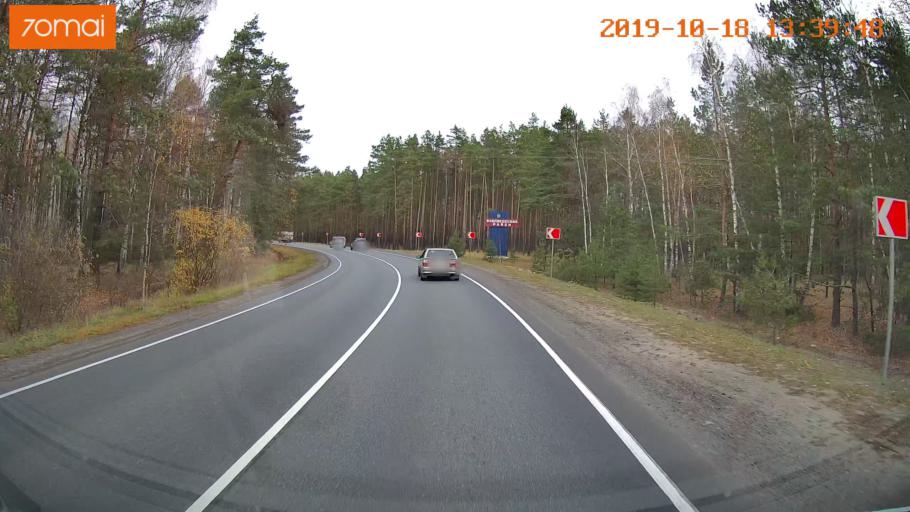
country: RU
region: Rjazan
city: Solotcha
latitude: 54.9029
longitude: 40.0033
